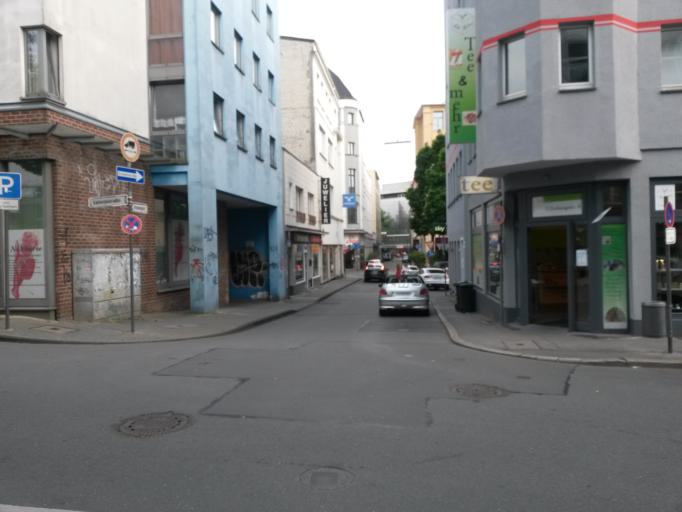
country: DE
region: North Rhine-Westphalia
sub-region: Regierungsbezirk Dusseldorf
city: Wuppertal
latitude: 51.2583
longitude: 7.1431
